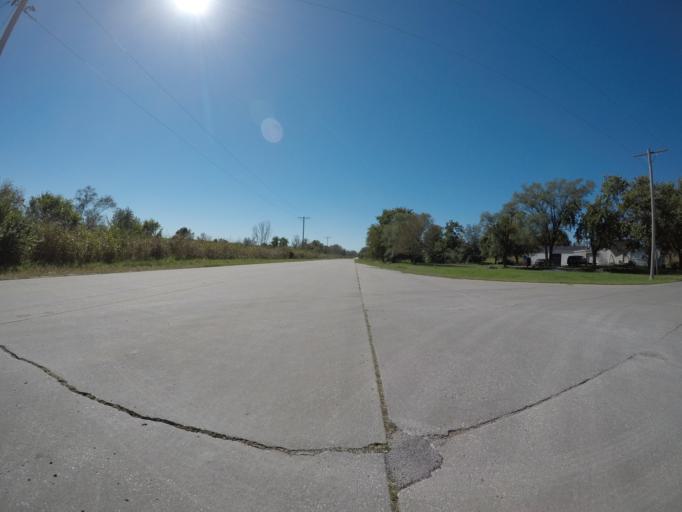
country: US
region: Kansas
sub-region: Wyandotte County
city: Bonner Springs
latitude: 39.0435
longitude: -94.8901
